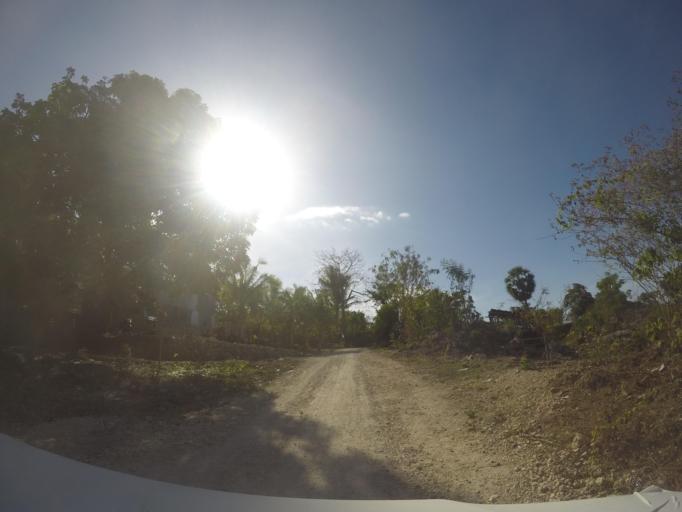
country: TL
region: Baucau
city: Baucau
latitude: -8.4552
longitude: 126.4434
